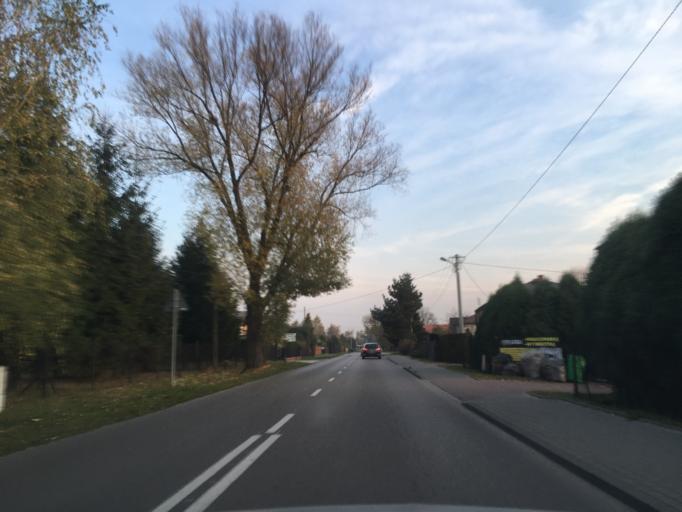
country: PL
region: Masovian Voivodeship
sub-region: Powiat piaseczynski
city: Lesznowola
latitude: 52.0542
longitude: 20.9255
